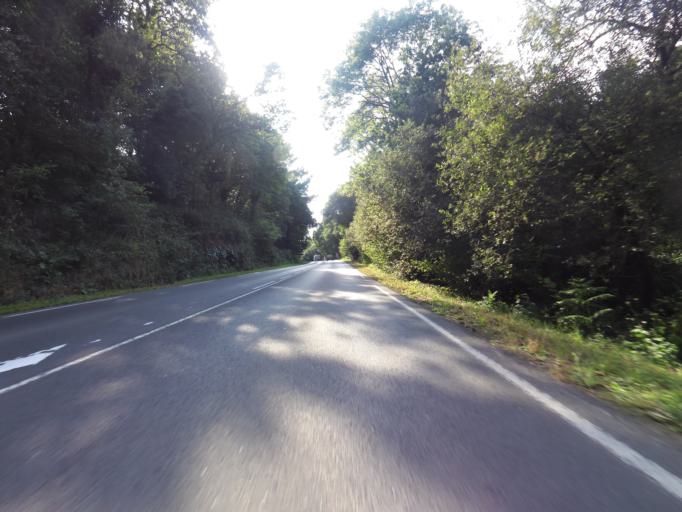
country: FR
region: Brittany
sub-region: Departement du Finistere
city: Pouldreuzic
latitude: 47.9702
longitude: -4.3774
